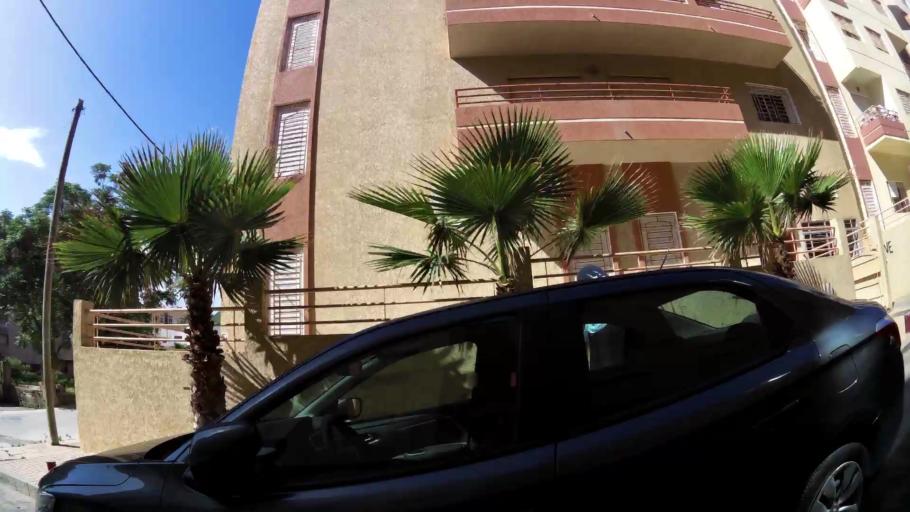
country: MA
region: Rabat-Sale-Zemmour-Zaer
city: Sale
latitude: 34.0690
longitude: -6.8022
